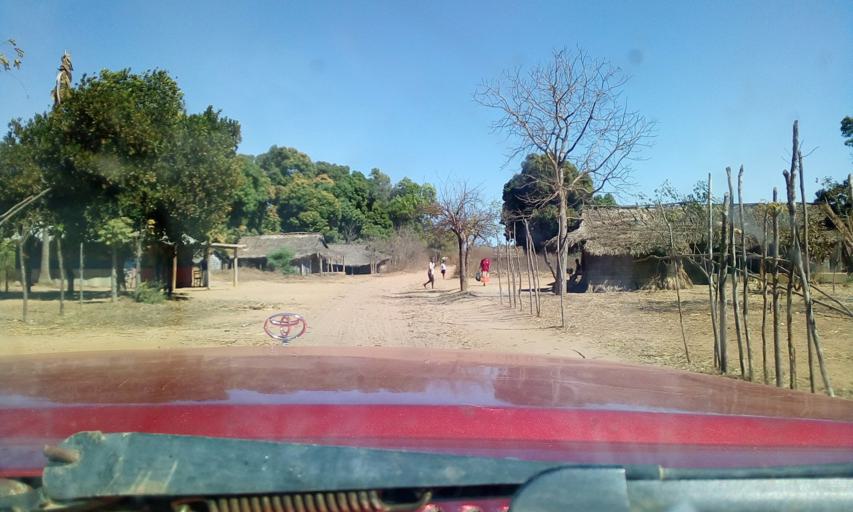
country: MG
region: Boeny
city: Mahajanga
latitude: -15.9620
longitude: 45.9458
